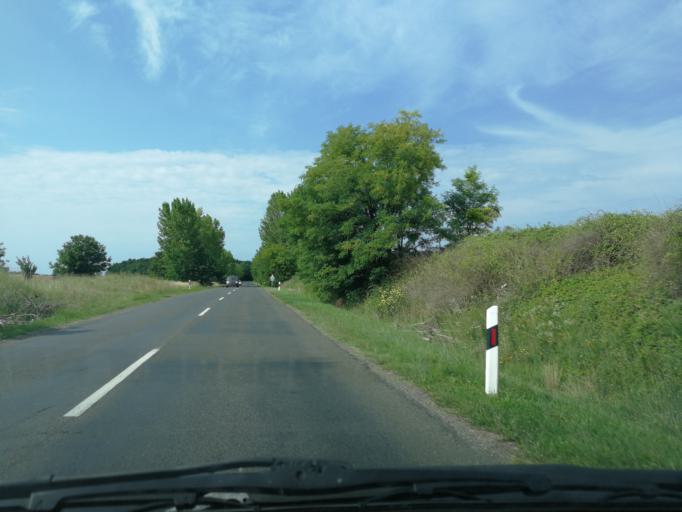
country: HU
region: Bacs-Kiskun
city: Davod
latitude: 46.0091
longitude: 18.9347
